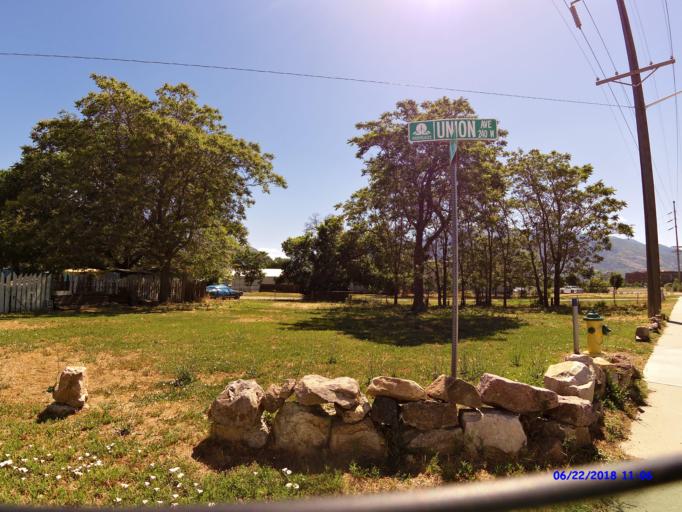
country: US
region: Utah
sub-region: Weber County
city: Ogden
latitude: 41.2277
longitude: -111.9829
